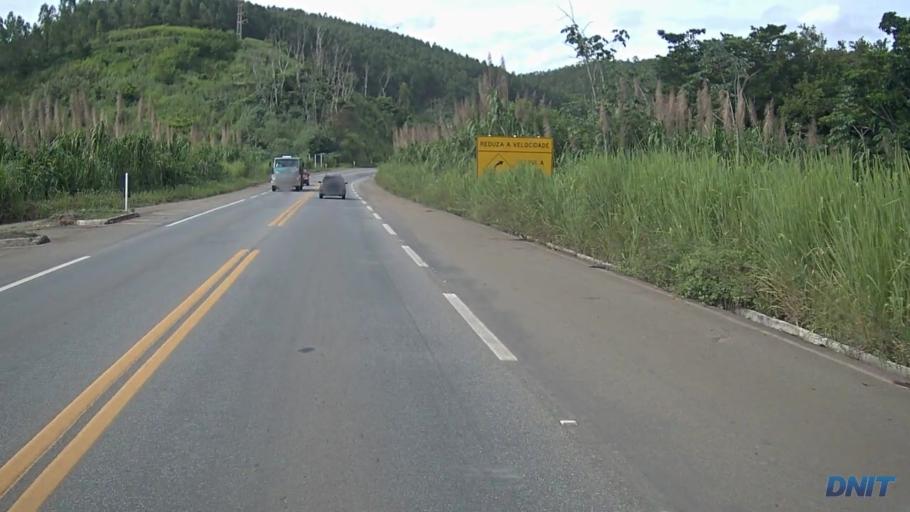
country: BR
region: Minas Gerais
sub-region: Ipaba
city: Ipaba
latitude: -19.3626
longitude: -42.4482
